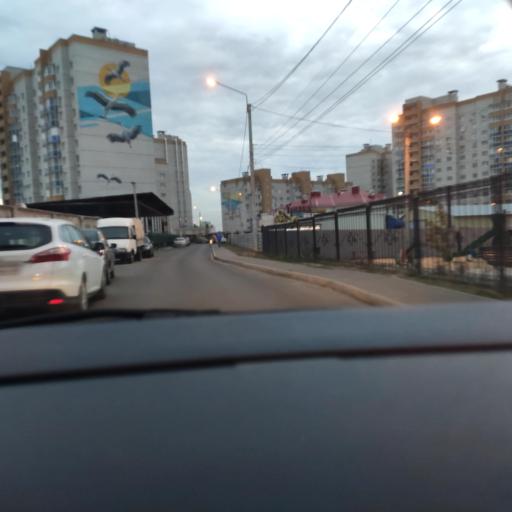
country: RU
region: Voronezj
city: Podgornoye
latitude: 51.7214
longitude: 39.1422
